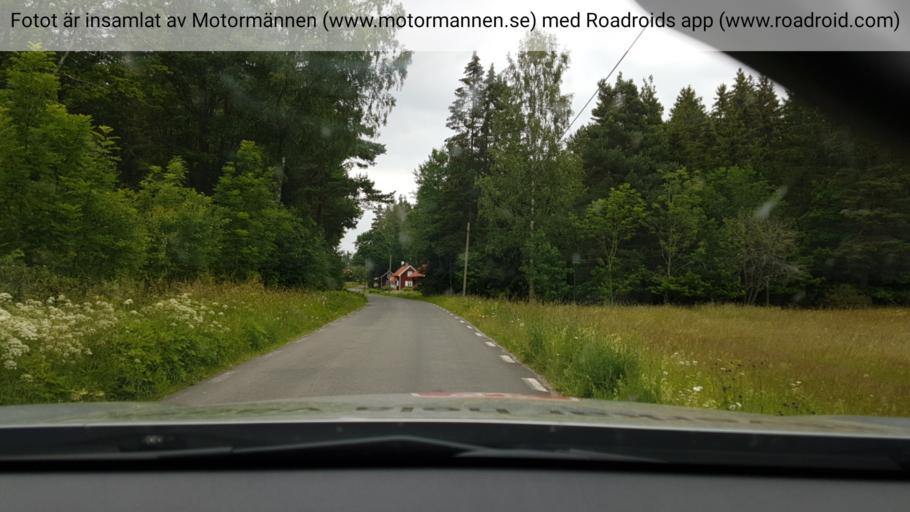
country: SE
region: Vaestra Goetaland
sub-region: Skovde Kommun
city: Skultorp
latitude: 58.2953
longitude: 13.8322
